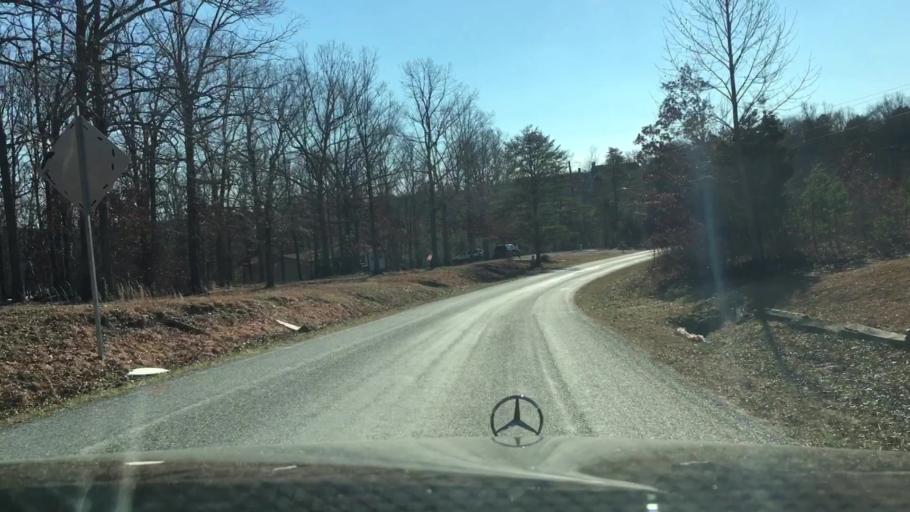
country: US
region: Virginia
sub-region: Campbell County
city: Altavista
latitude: 37.1815
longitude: -79.3199
